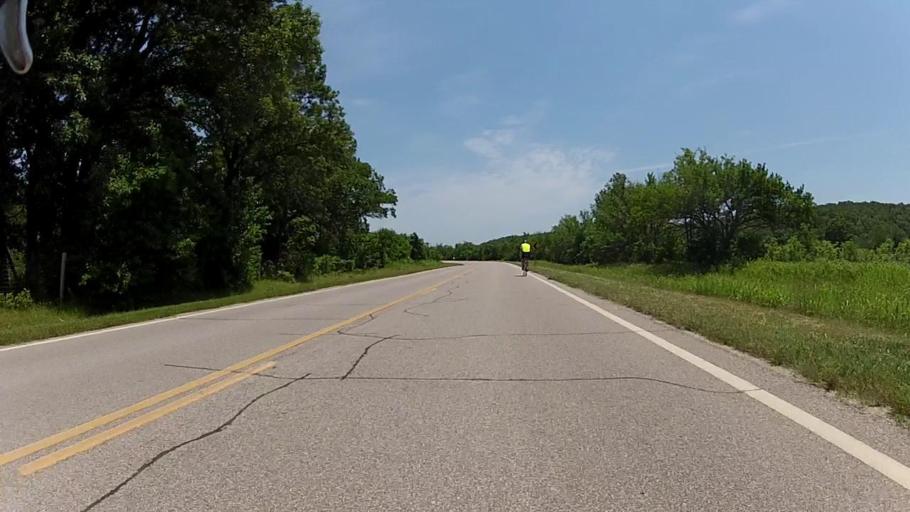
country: US
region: Kansas
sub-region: Chautauqua County
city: Sedan
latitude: 37.1193
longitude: -96.2216
